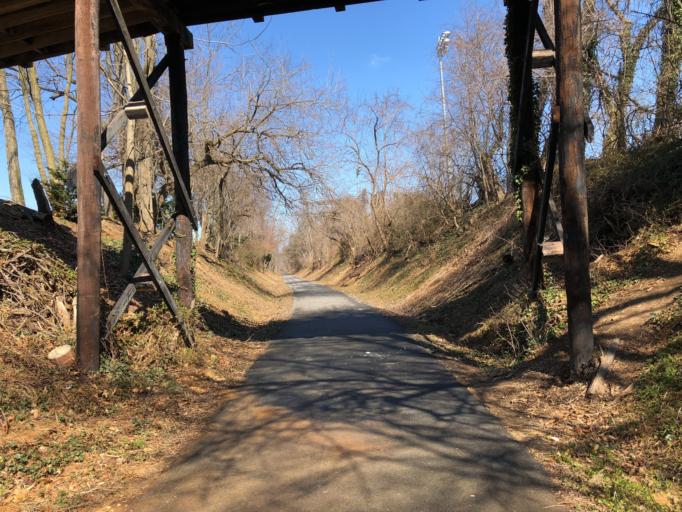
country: US
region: Maryland
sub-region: Kent County
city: Chestertown
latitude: 39.2176
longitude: -76.0712
